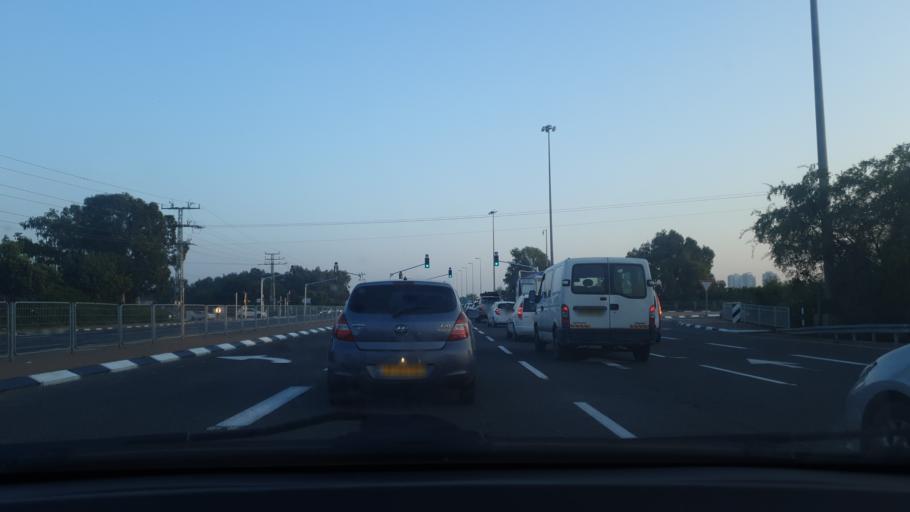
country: IL
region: Central District
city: Ramla
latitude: 31.9524
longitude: 34.8561
